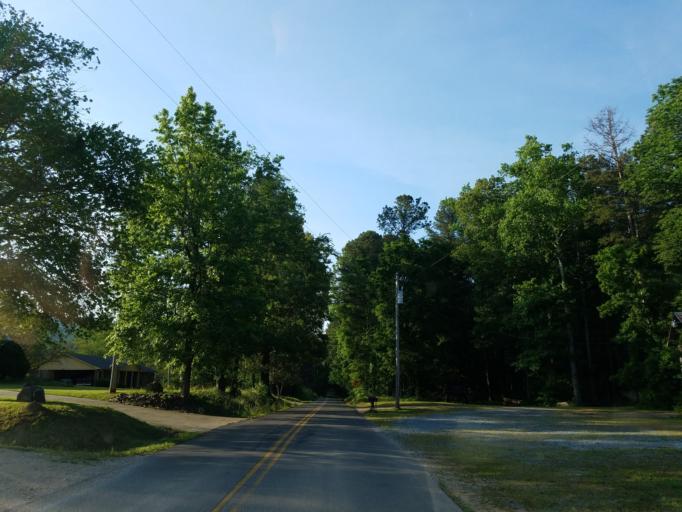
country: US
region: Georgia
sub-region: Gordon County
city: Calhoun
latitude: 34.5124
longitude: -85.1200
